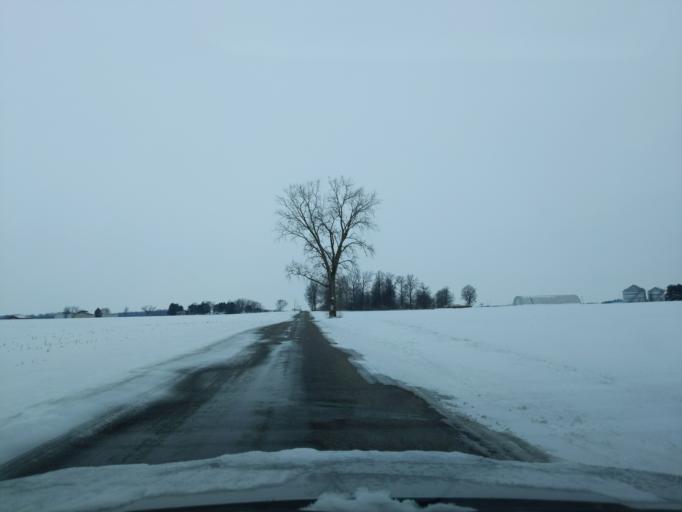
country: US
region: Indiana
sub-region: Benton County
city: Otterbein
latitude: 40.4397
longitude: -87.0927
